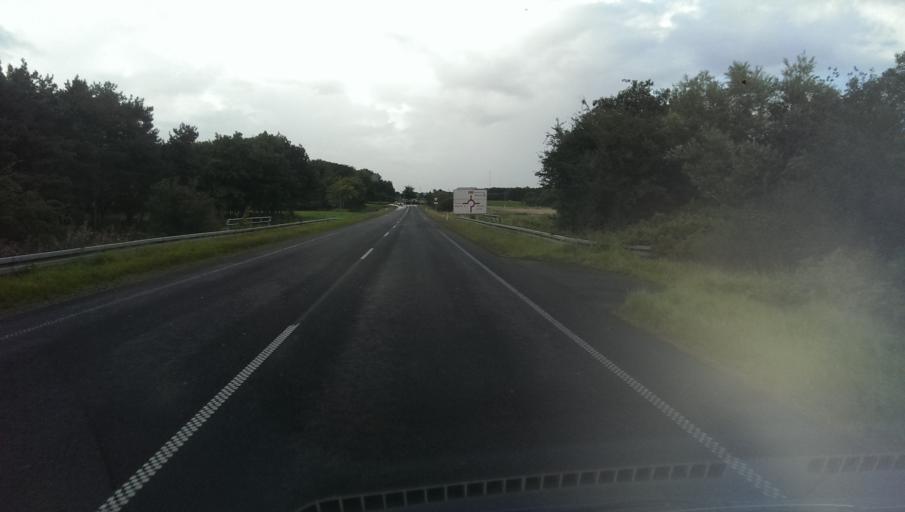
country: DK
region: South Denmark
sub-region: Varde Kommune
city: Olgod
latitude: 55.8017
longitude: 8.6289
